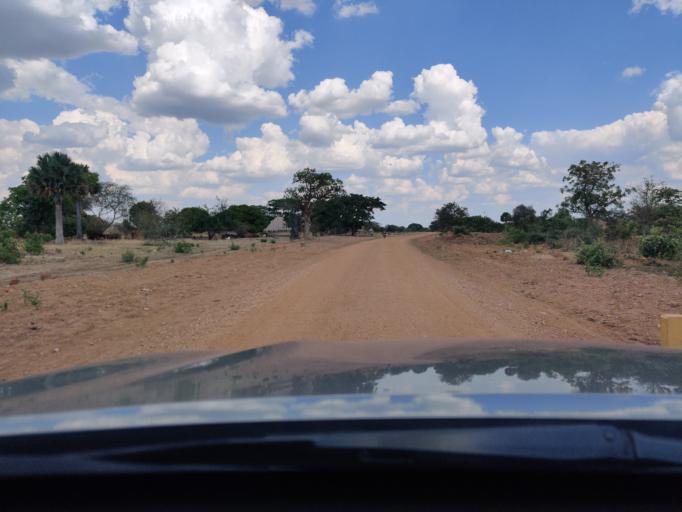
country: ZM
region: Central
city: Chibombo
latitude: -14.7603
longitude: 27.8867
